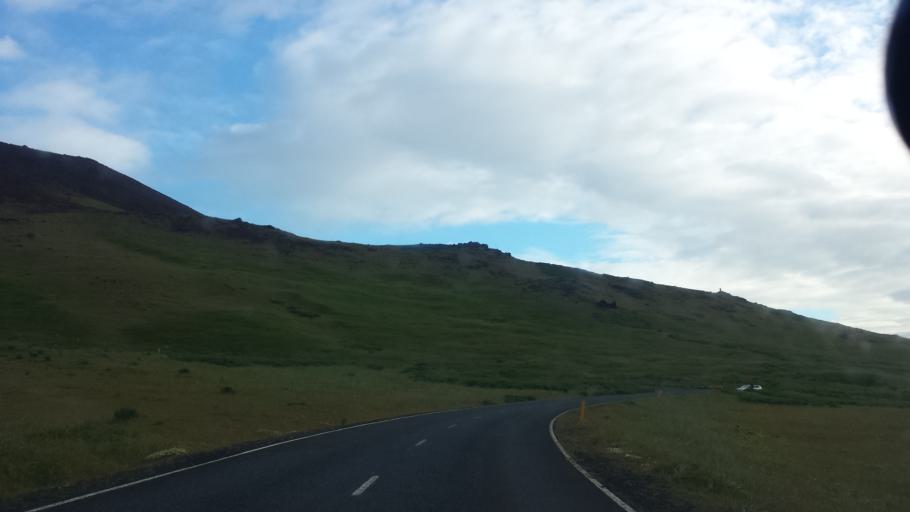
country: IS
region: South
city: Vestmannaeyjar
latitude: 63.4340
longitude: -20.2591
